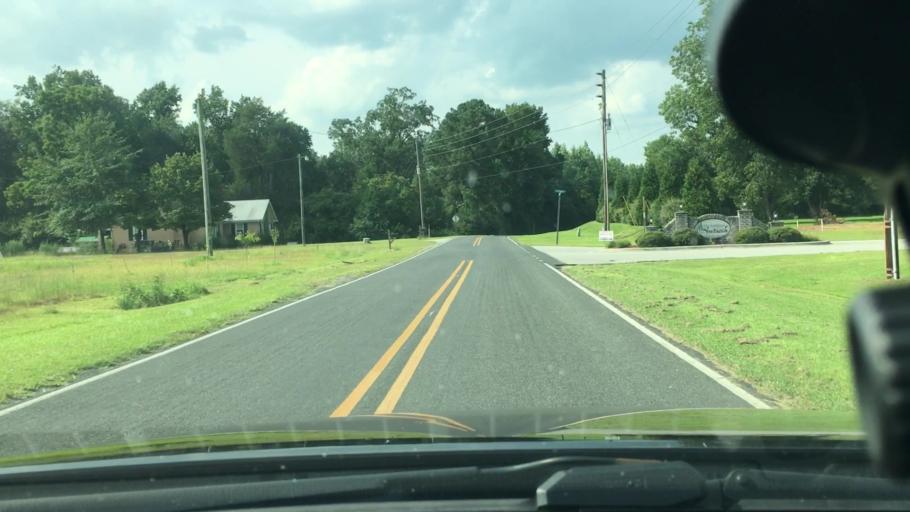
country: US
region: North Carolina
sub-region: Craven County
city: New Bern
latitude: 35.1836
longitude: -77.0579
